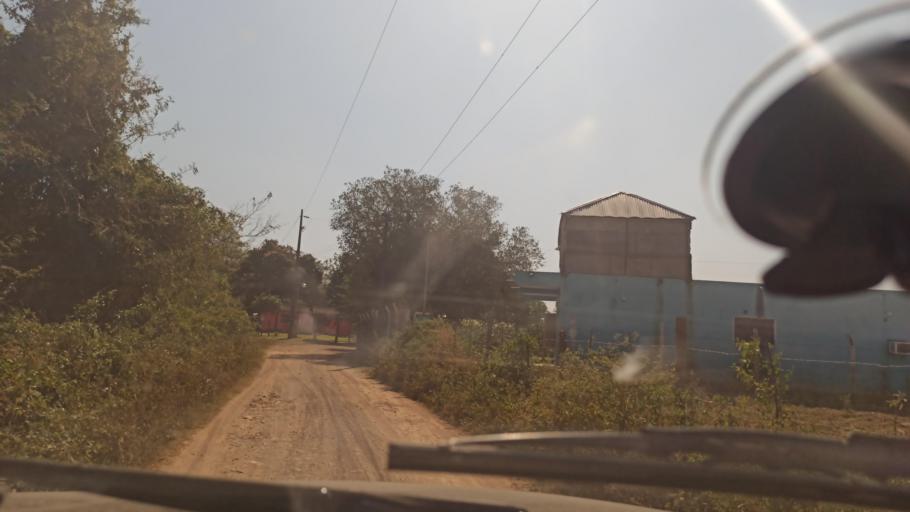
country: AR
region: Formosa
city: Clorinda
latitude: -25.3150
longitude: -57.6992
